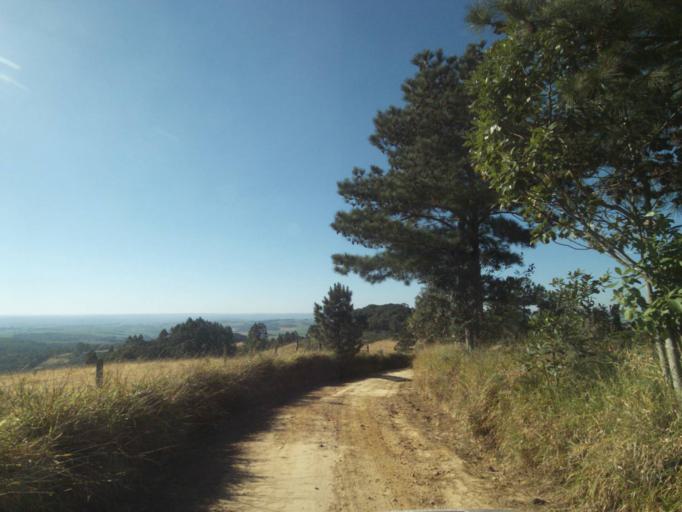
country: BR
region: Parana
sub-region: Tibagi
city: Tibagi
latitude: -24.5503
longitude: -50.4709
